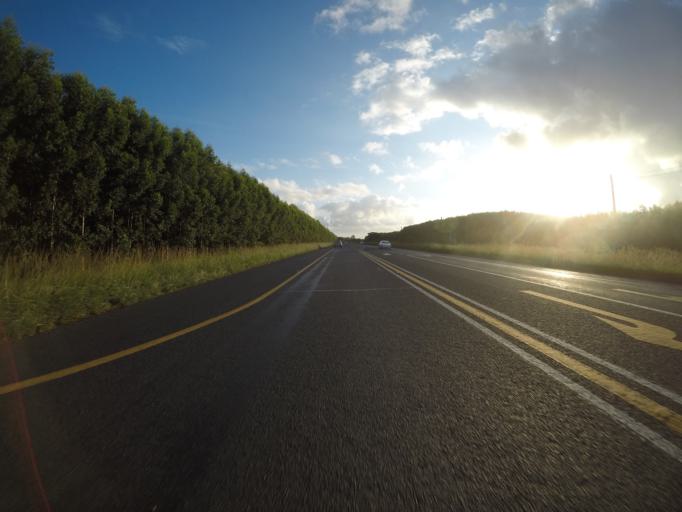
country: ZA
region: KwaZulu-Natal
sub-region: uThungulu District Municipality
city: KwaMbonambi
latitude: -28.6231
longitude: 32.0736
